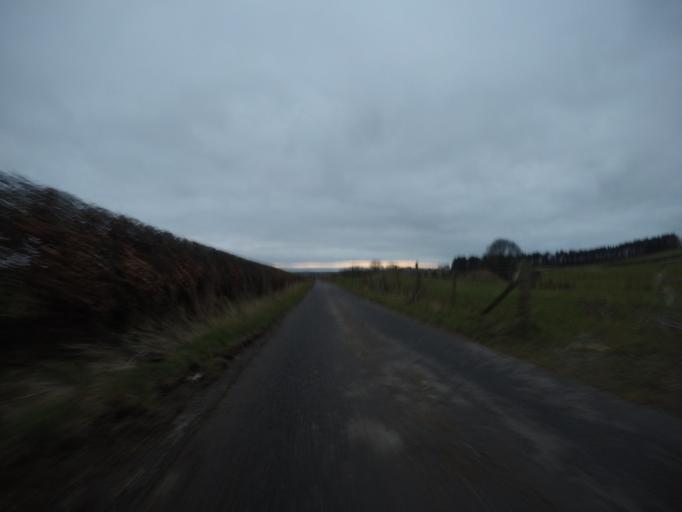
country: GB
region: Scotland
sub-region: North Ayrshire
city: Dalry
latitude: 55.6803
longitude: -4.7261
